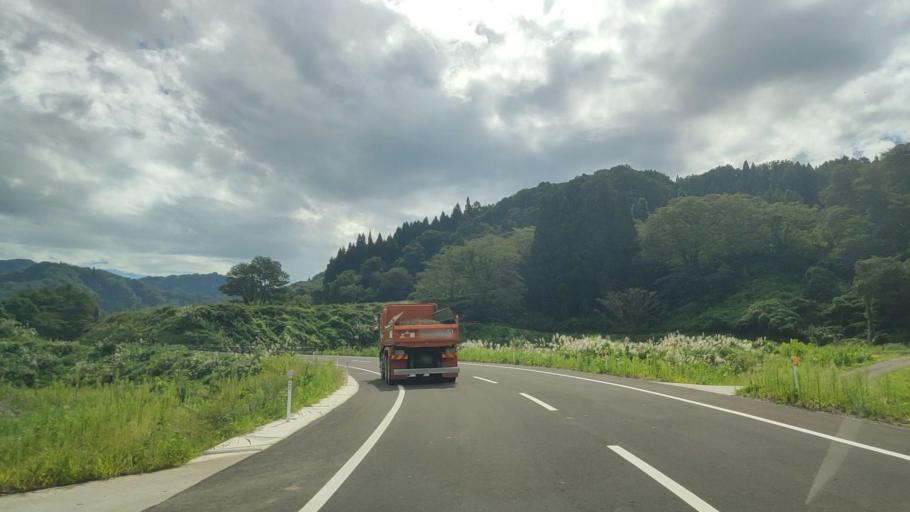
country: JP
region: Niigata
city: Arai
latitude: 36.9495
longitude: 138.2815
